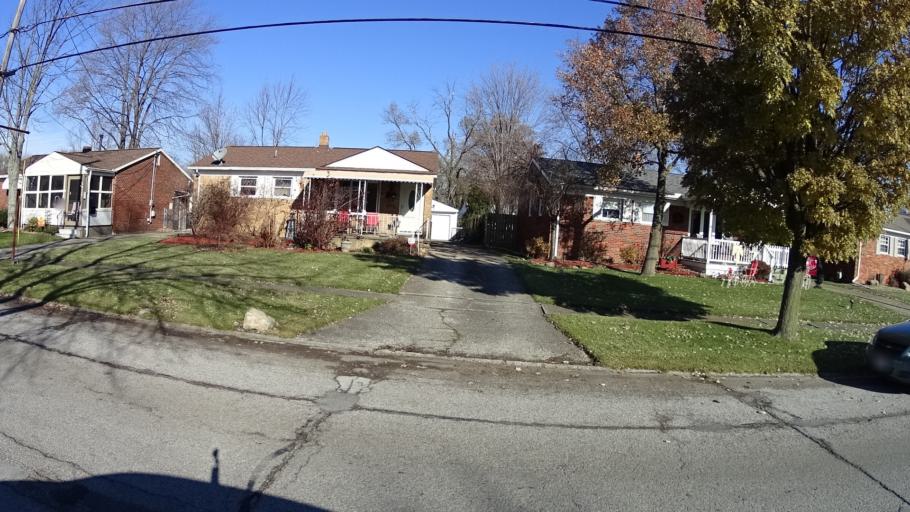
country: US
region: Ohio
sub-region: Lorain County
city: Sheffield
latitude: 41.3966
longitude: -82.0765
